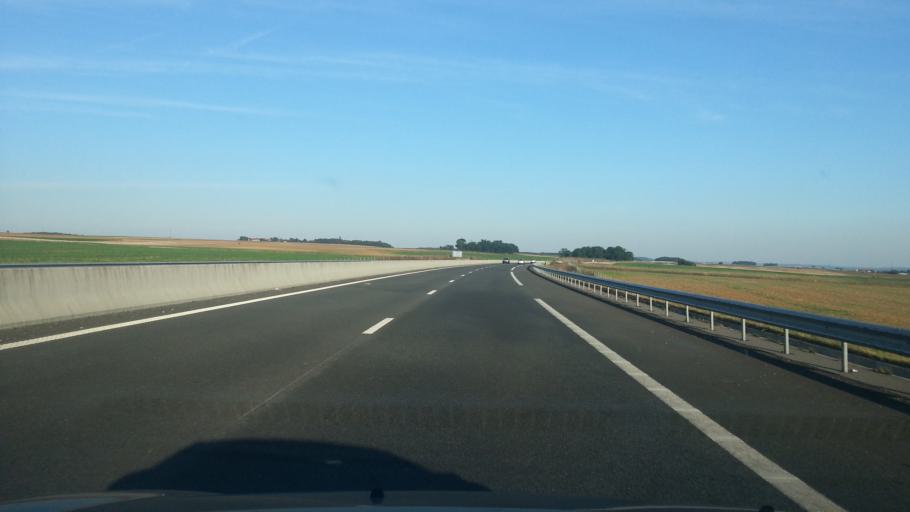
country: FR
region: Picardie
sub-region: Departement de l'Oise
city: Catenoy
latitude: 49.3849
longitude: 2.4888
